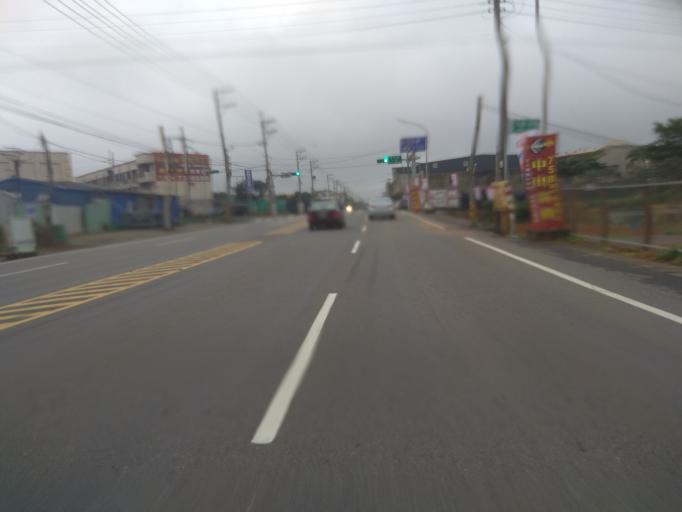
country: TW
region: Taiwan
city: Taoyuan City
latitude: 25.0287
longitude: 121.1076
